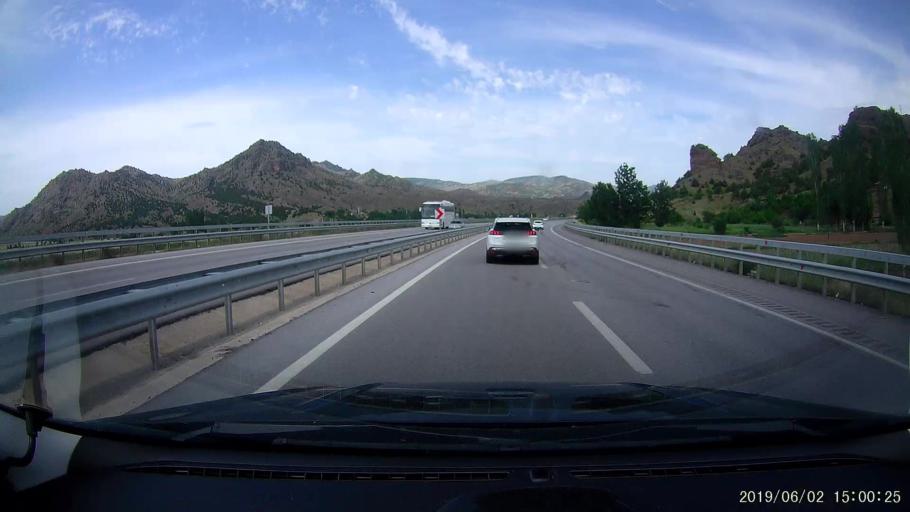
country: TR
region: Corum
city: Osmancik
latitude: 40.9788
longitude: 34.7122
